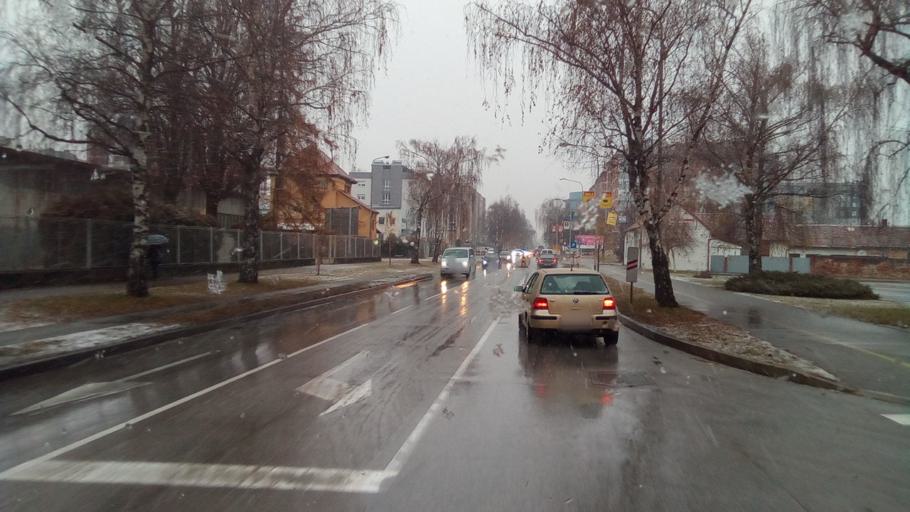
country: HR
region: Varazdinska
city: Varazdin
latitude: 46.2957
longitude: 16.3421
